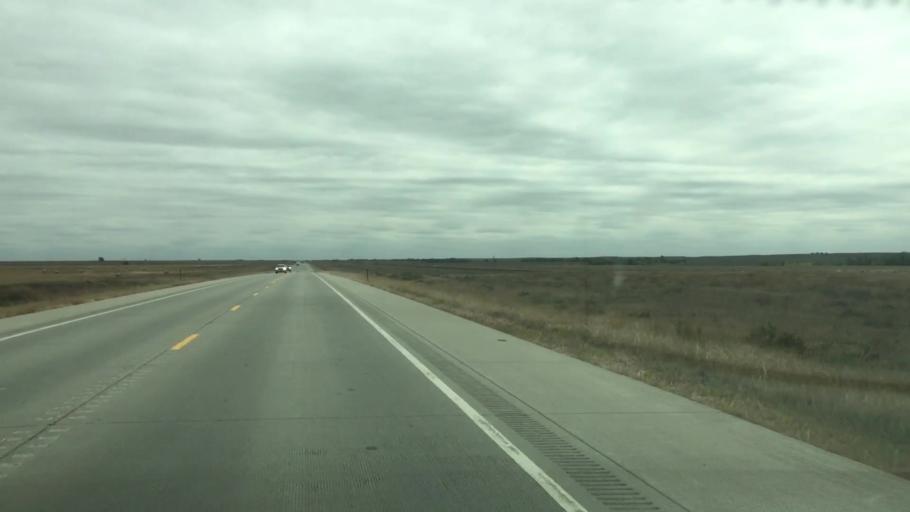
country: US
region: Colorado
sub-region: Kiowa County
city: Eads
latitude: 38.7737
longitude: -102.8771
